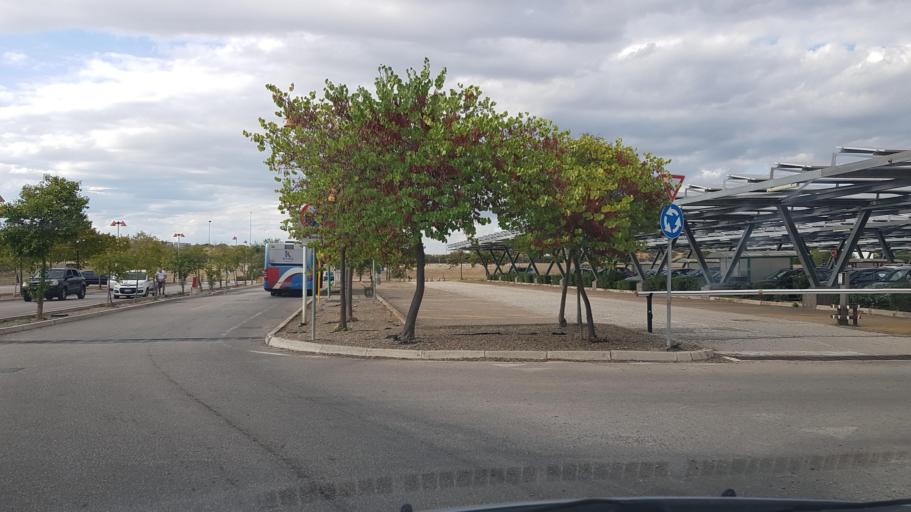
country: IT
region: Apulia
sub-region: Provincia di Taranto
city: Paolo VI
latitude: 40.5174
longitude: 17.2899
